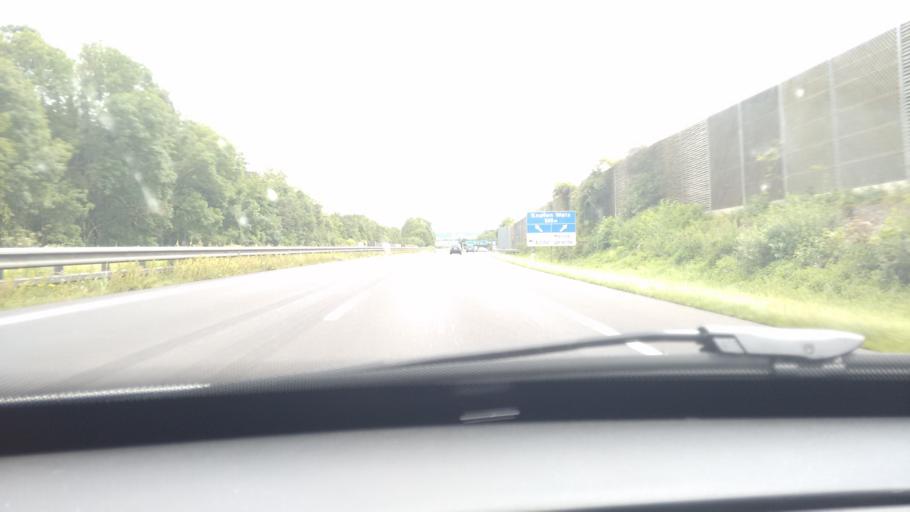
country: AT
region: Upper Austria
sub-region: Wels-Land
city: Gunskirchen
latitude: 48.1849
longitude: 13.9580
